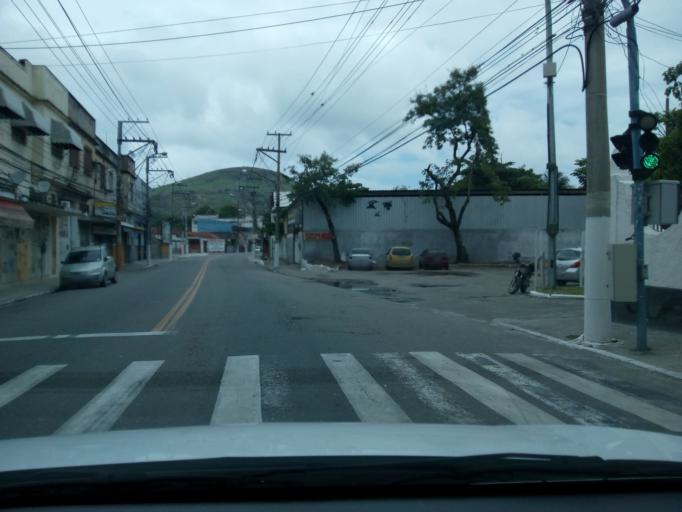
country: BR
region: Rio de Janeiro
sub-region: Niteroi
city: Niteroi
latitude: -22.8639
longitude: -43.1037
